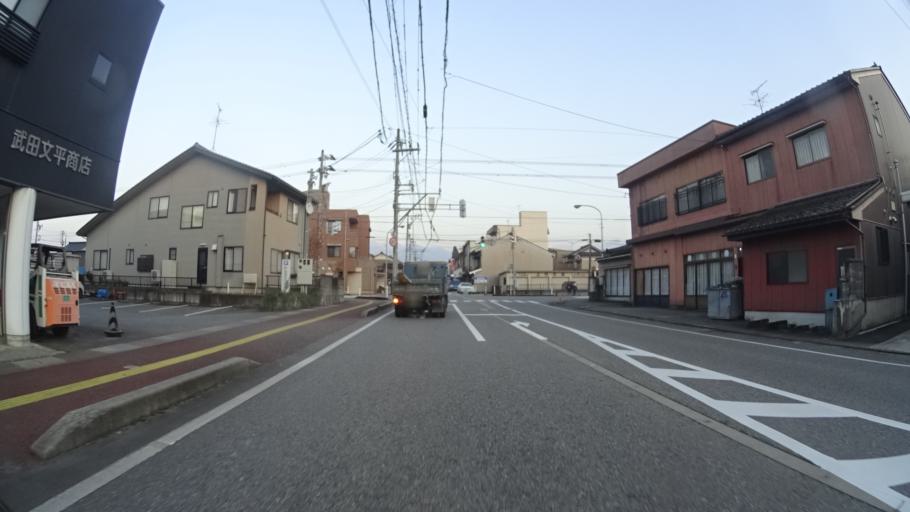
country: JP
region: Toyama
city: Kamiichi
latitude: 36.7065
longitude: 137.3585
